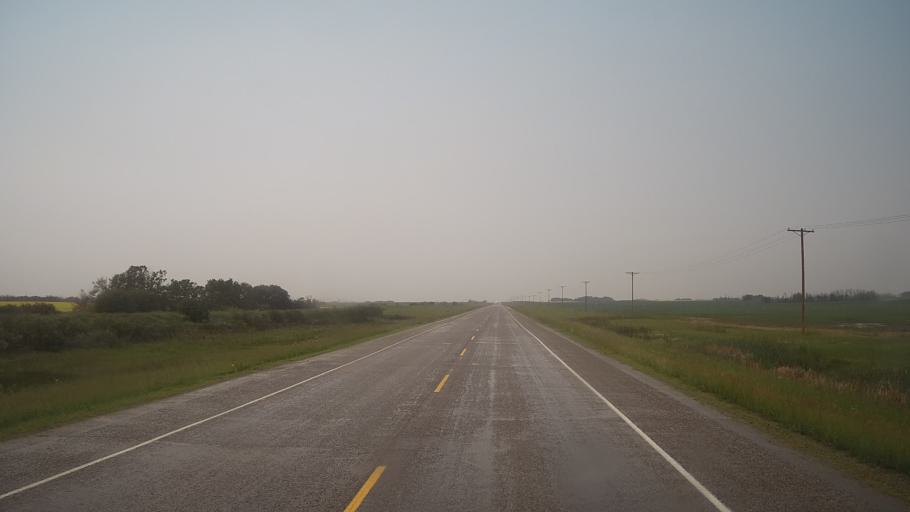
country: CA
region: Saskatchewan
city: Biggar
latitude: 52.1534
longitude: -108.2443
